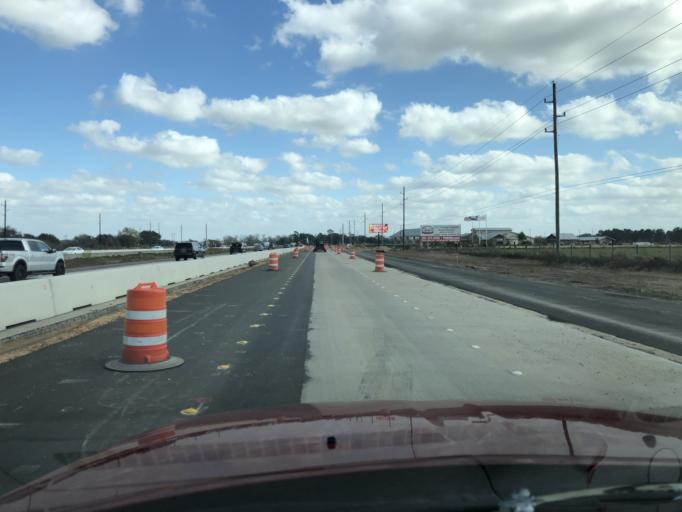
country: US
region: Texas
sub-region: Waller County
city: Brookshire
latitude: 29.7701
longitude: -96.0497
